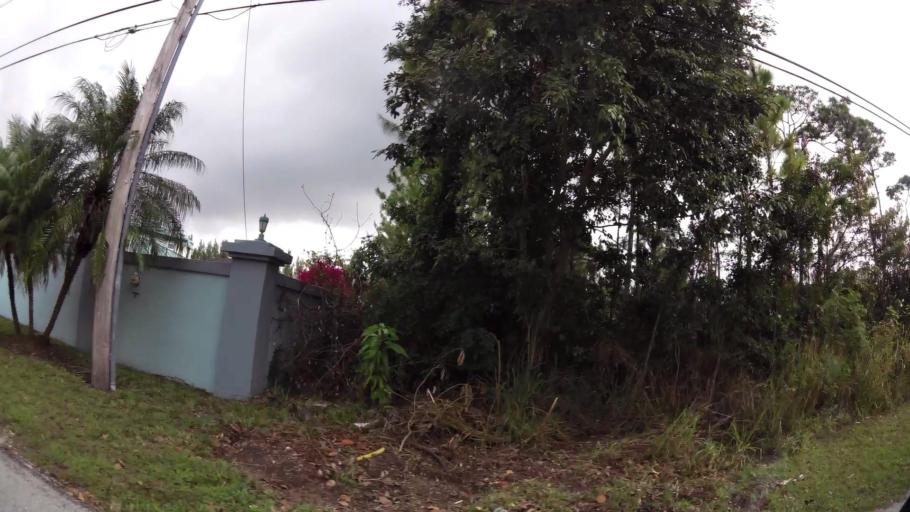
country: BS
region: Freeport
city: Lucaya
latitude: 26.5705
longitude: -78.5750
